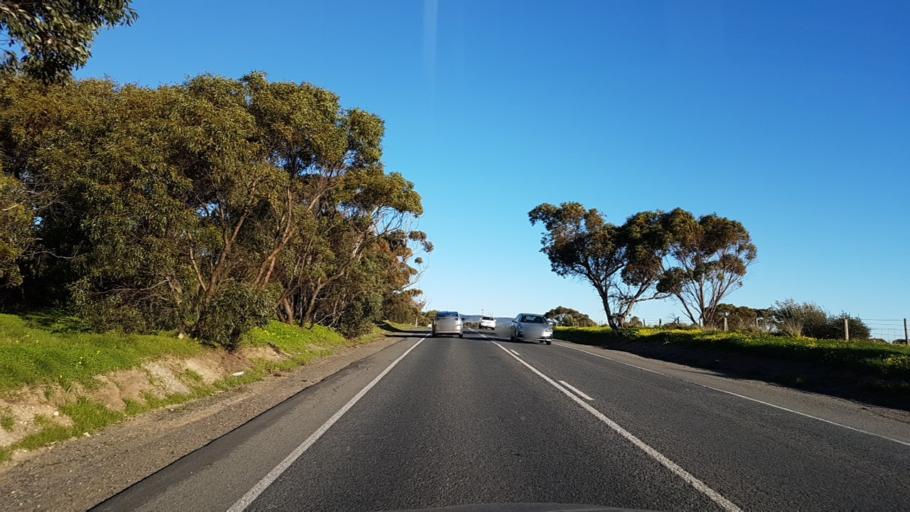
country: AU
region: South Australia
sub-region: Onkaparinga
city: Aldinga
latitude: -35.2483
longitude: 138.4945
